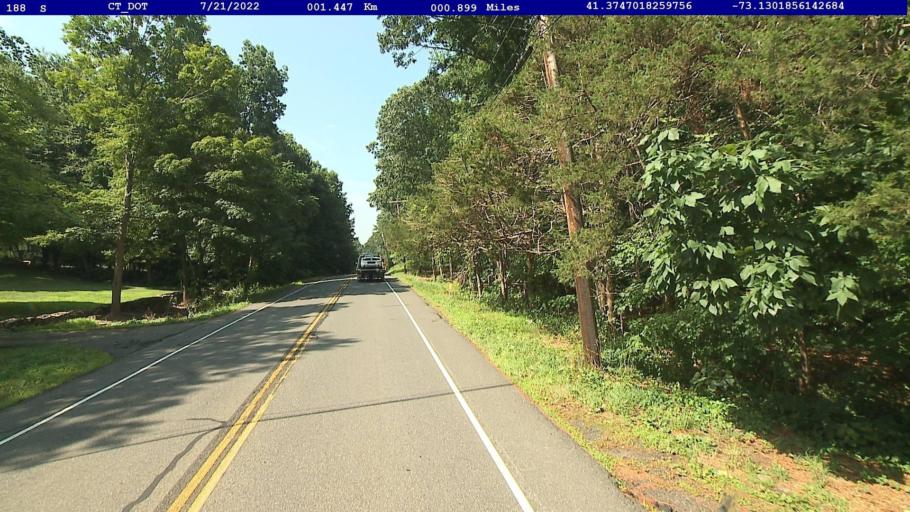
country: US
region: Connecticut
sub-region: New Haven County
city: Seymour
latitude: 41.3748
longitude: -73.1301
